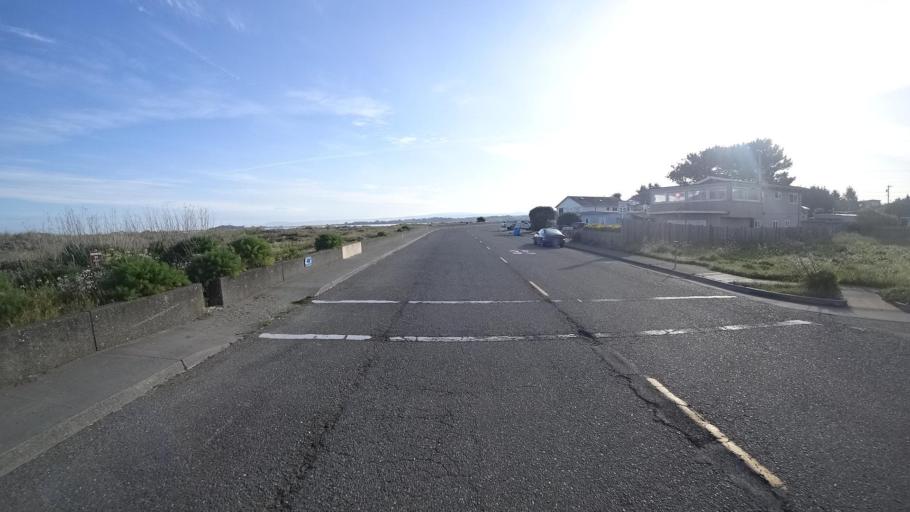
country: US
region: California
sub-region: Humboldt County
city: Humboldt Hill
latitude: 40.7410
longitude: -124.2172
